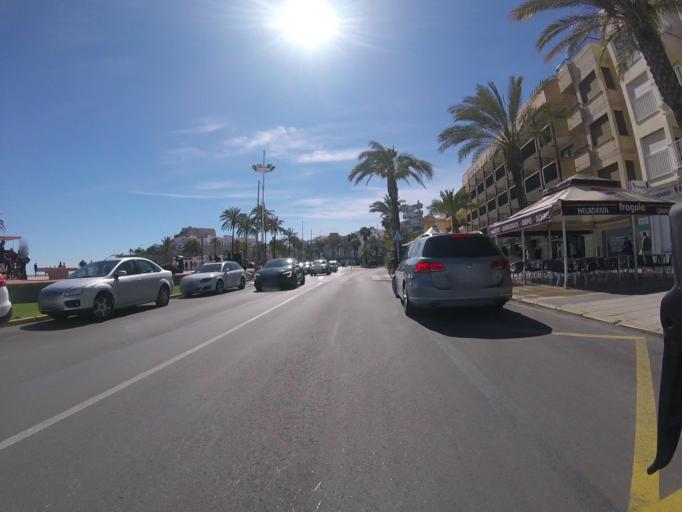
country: ES
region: Valencia
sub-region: Provincia de Castello
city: Peniscola
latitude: 40.3608
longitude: 0.4026
